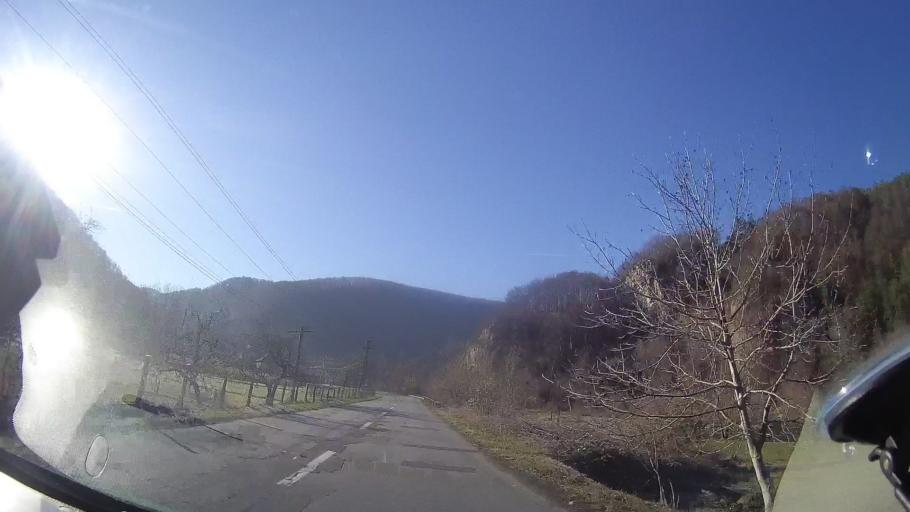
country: RO
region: Bihor
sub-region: Comuna Bulz
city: Bulz
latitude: 46.9279
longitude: 22.6581
